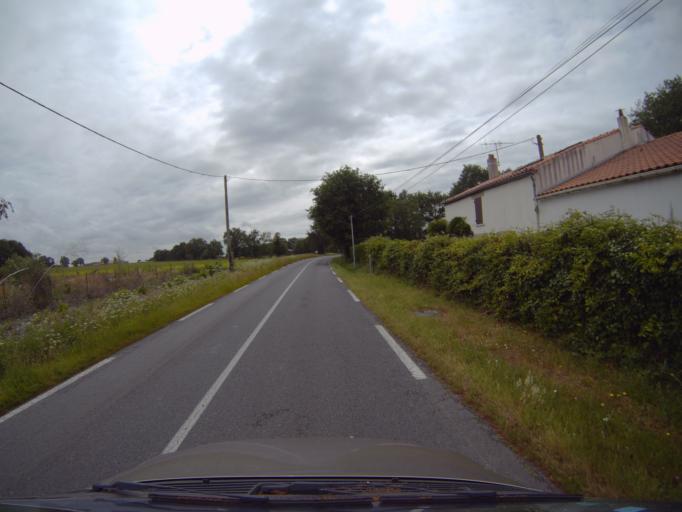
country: FR
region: Pays de la Loire
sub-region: Departement de la Loire-Atlantique
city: Aigrefeuille-sur-Maine
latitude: 47.0618
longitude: -1.4397
